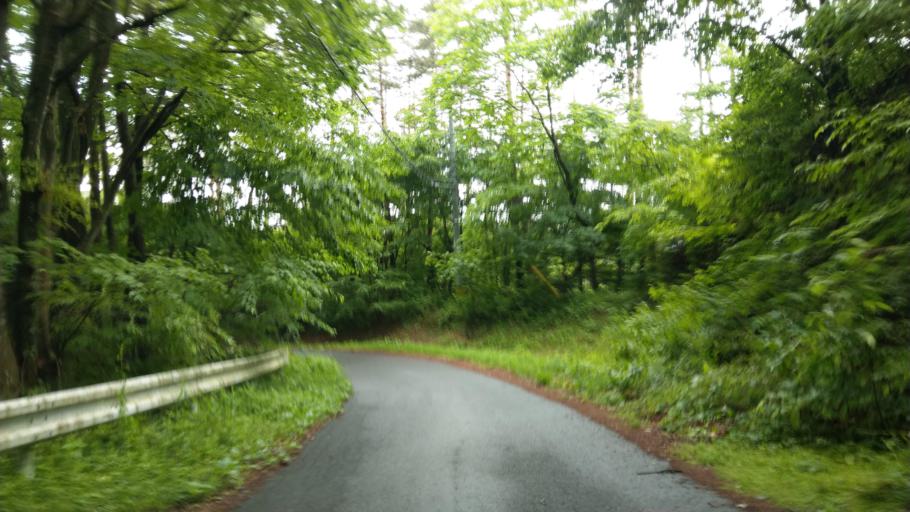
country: JP
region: Nagano
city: Komoro
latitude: 36.2769
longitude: 138.3720
